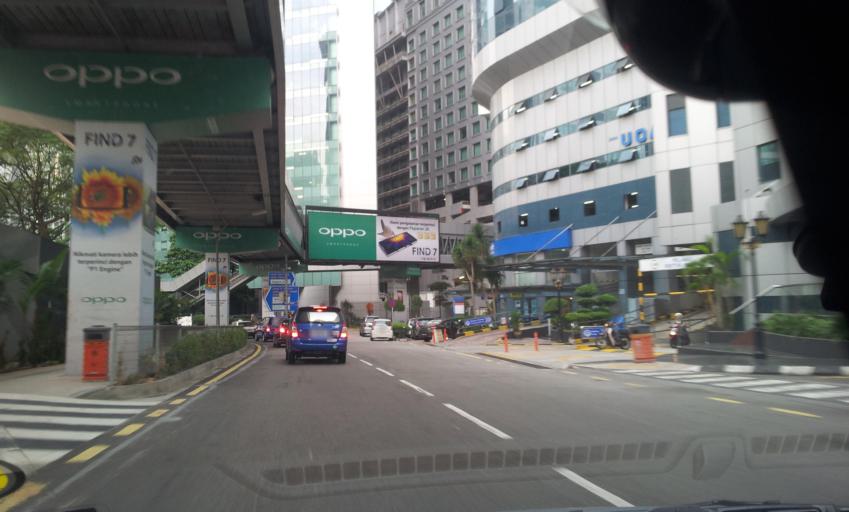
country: MY
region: Kuala Lumpur
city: Kuala Lumpur
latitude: 3.1519
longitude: 101.7123
